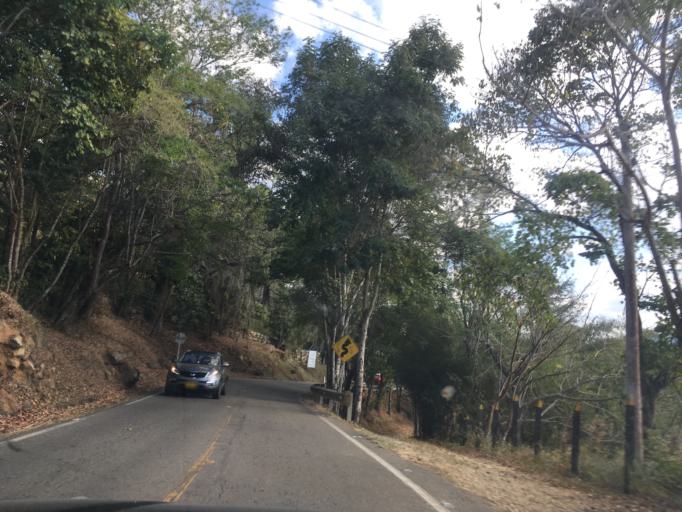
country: CO
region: Santander
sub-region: San Gil
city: San Gil
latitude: 6.5789
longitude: -73.1553
